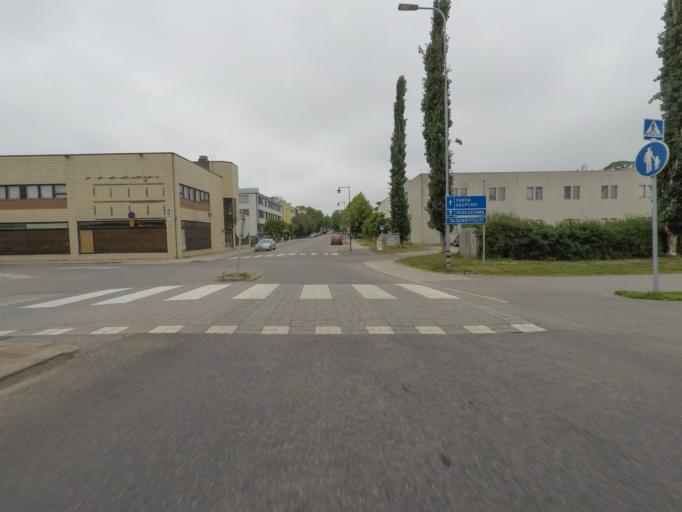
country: FI
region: Varsinais-Suomi
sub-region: Turku
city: Naantali
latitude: 60.4686
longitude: 22.0270
